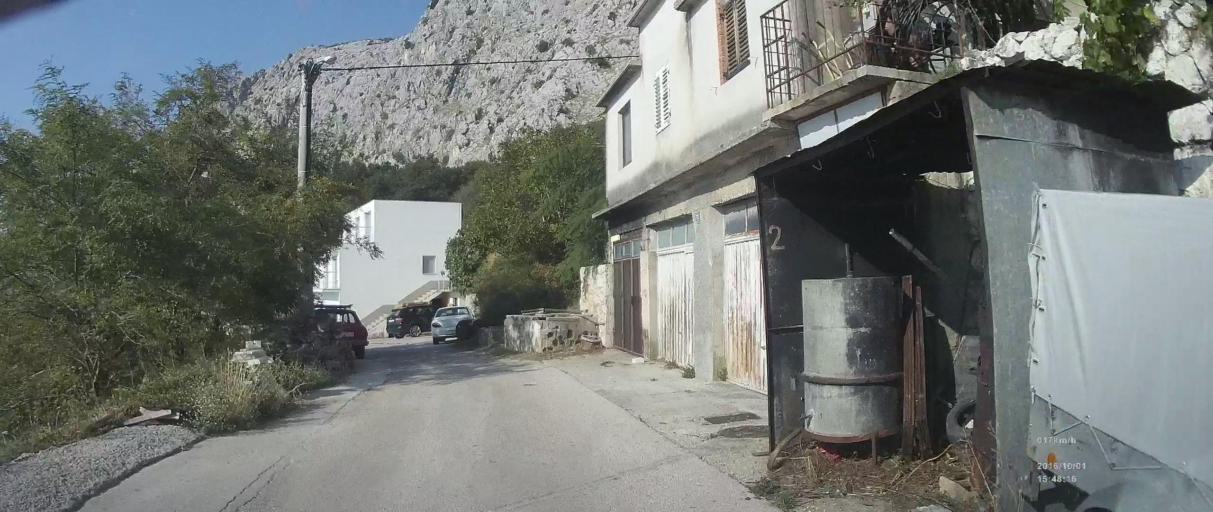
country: HR
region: Splitsko-Dalmatinska
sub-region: Grad Omis
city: Omis
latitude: 43.4370
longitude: 16.7085
